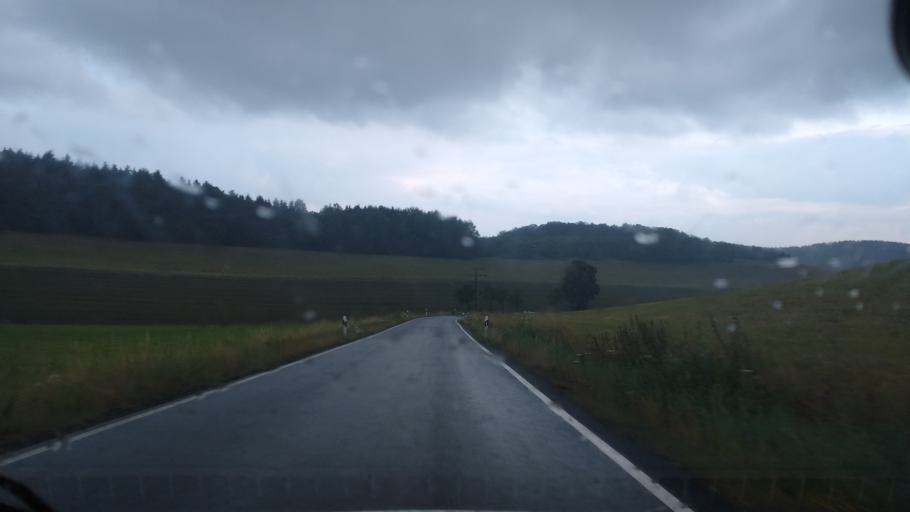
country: DE
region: Hesse
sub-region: Regierungsbezirk Darmstadt
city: Erbach
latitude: 49.6525
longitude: 8.9453
